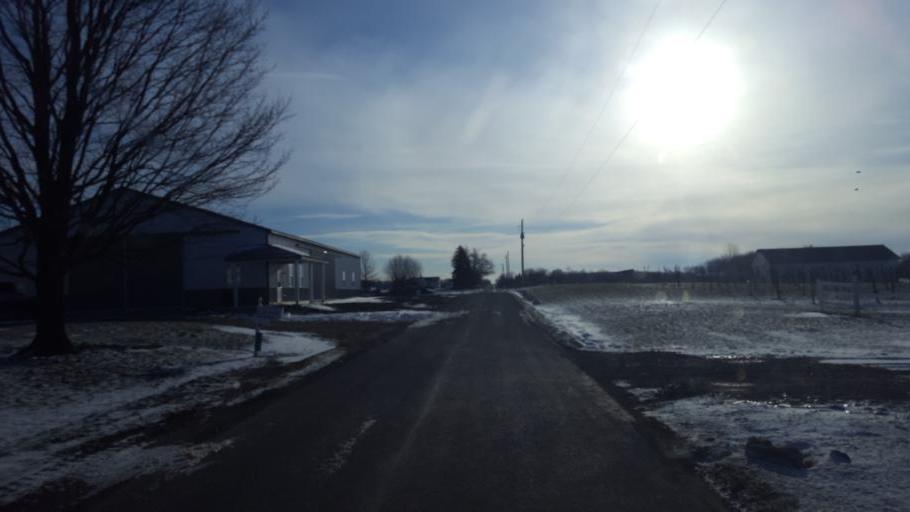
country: US
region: Ohio
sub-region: Morrow County
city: Mount Gilead
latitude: 40.6253
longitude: -82.8349
